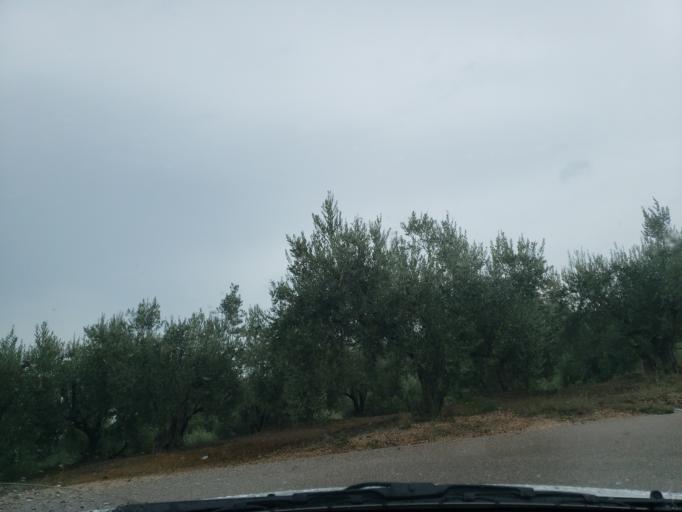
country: GR
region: Central Greece
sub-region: Nomos Fthiotidos
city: Anthili
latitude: 38.7957
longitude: 22.4838
